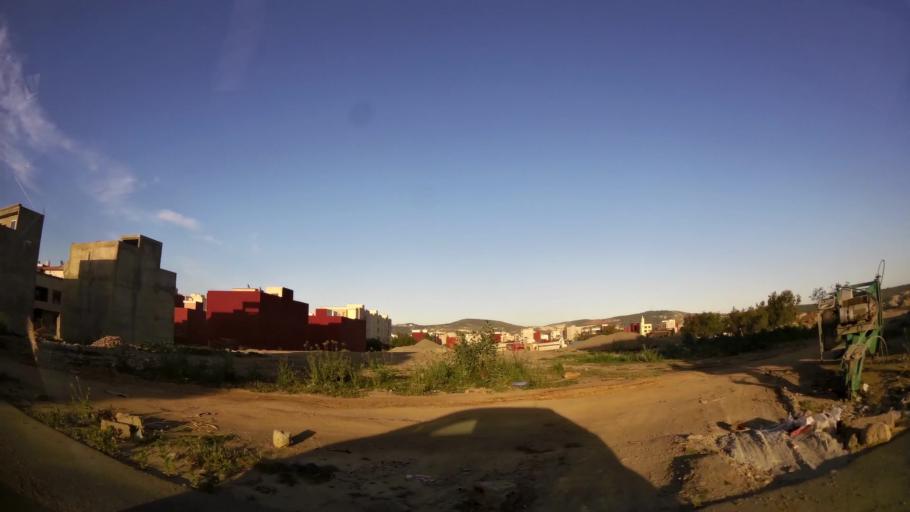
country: MA
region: Oriental
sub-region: Berkane-Taourirt
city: Madagh
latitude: 35.0765
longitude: -2.2351
